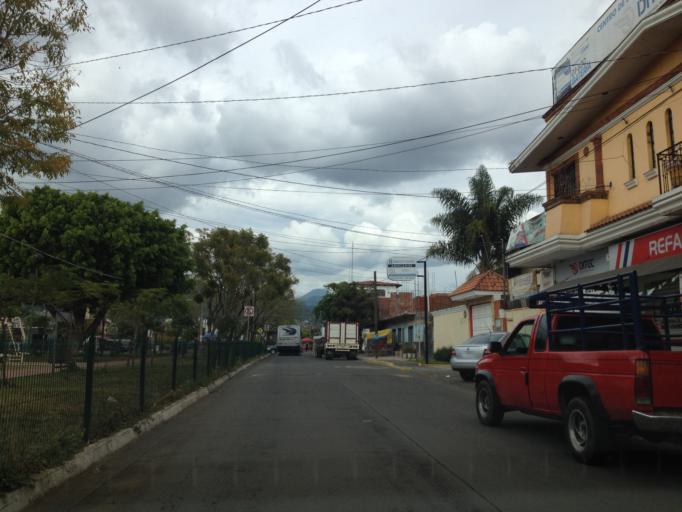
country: MX
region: Michoacan
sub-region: Uruapan
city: Uruapan
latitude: 19.4135
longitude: -102.0374
